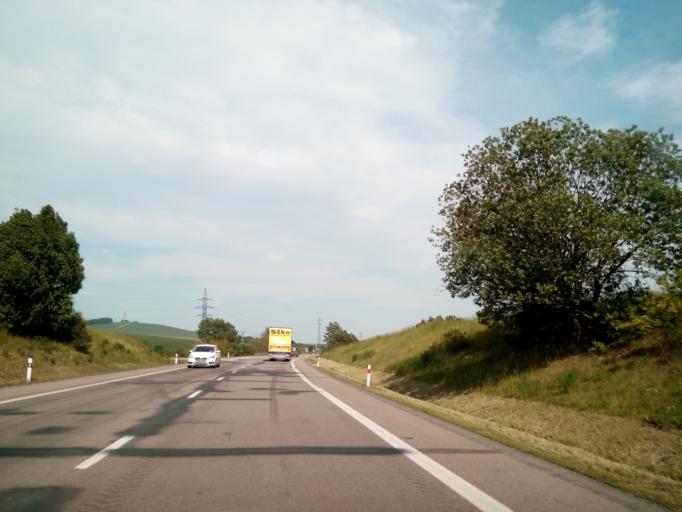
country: CZ
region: South Moravian
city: Slavkov u Brna
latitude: 49.1505
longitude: 16.9043
